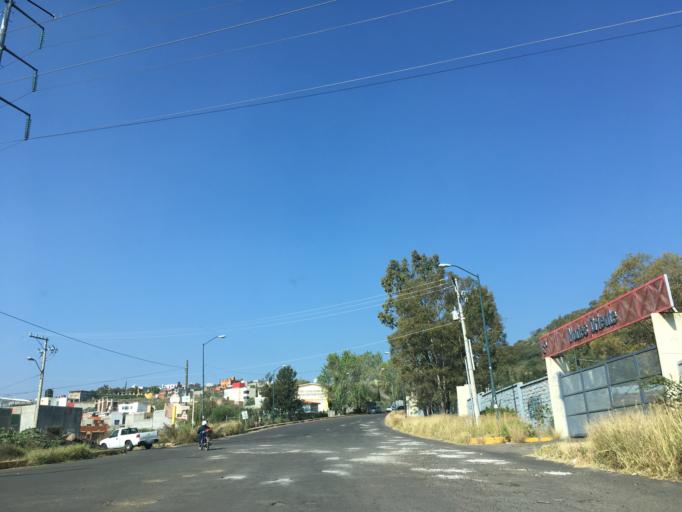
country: MX
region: Michoacan
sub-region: Tarimbaro
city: Fraccionamiento Metropolis II
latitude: 19.7165
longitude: -101.2330
